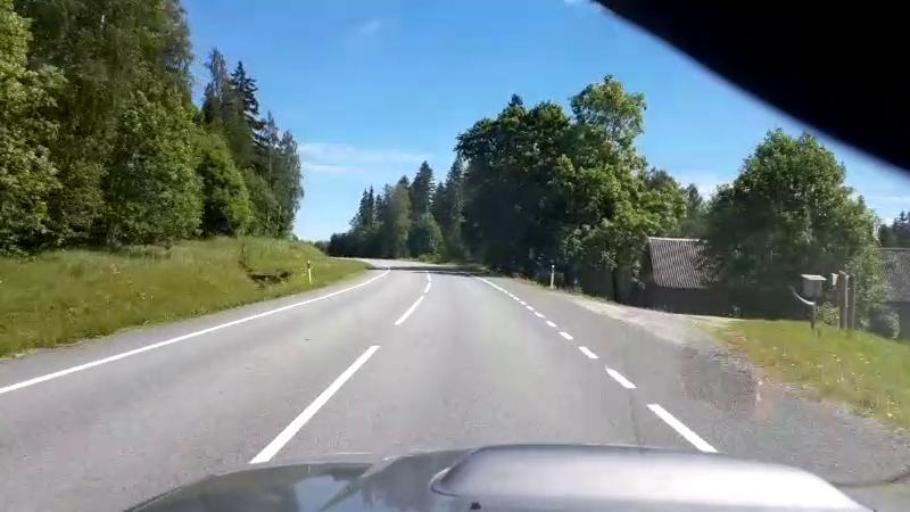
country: EE
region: Jaervamaa
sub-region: Jaerva-Jaani vald
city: Jarva-Jaani
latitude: 58.9972
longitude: 25.9435
